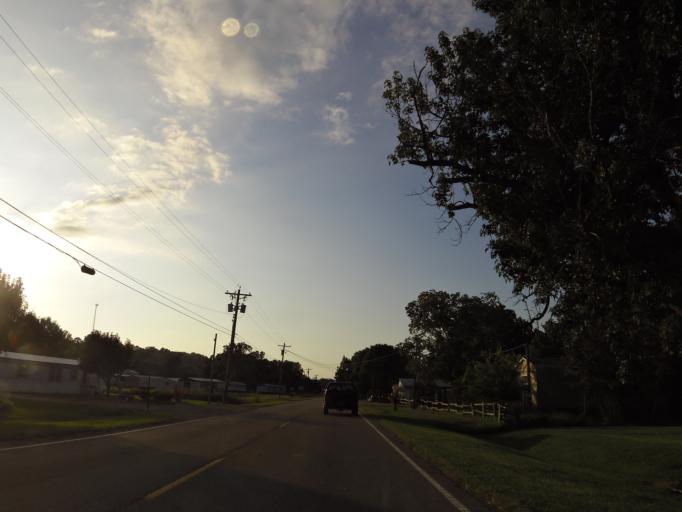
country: US
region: Tennessee
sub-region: Cocke County
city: Newport
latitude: 35.9777
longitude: -83.2772
